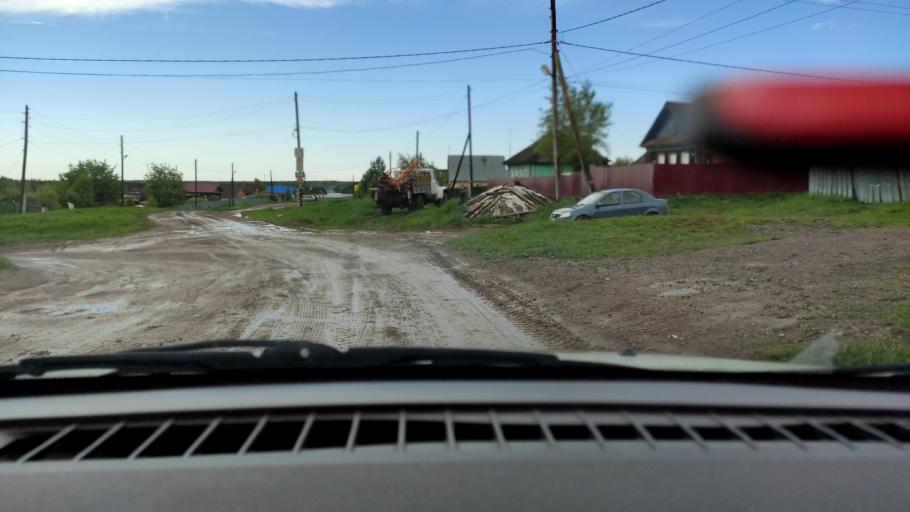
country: RU
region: Perm
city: Bershet'
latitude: 57.7283
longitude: 56.3781
